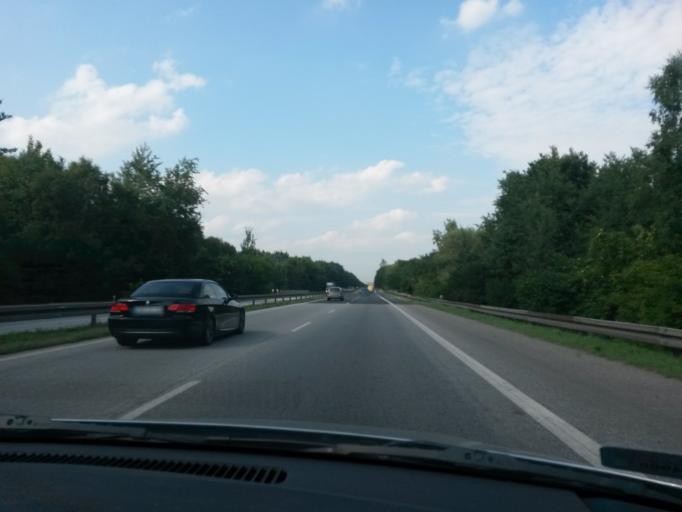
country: PL
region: Silesian Voivodeship
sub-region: Dabrowa Gornicza
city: Dabrowa Gornicza
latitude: 50.2969
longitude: 19.2205
